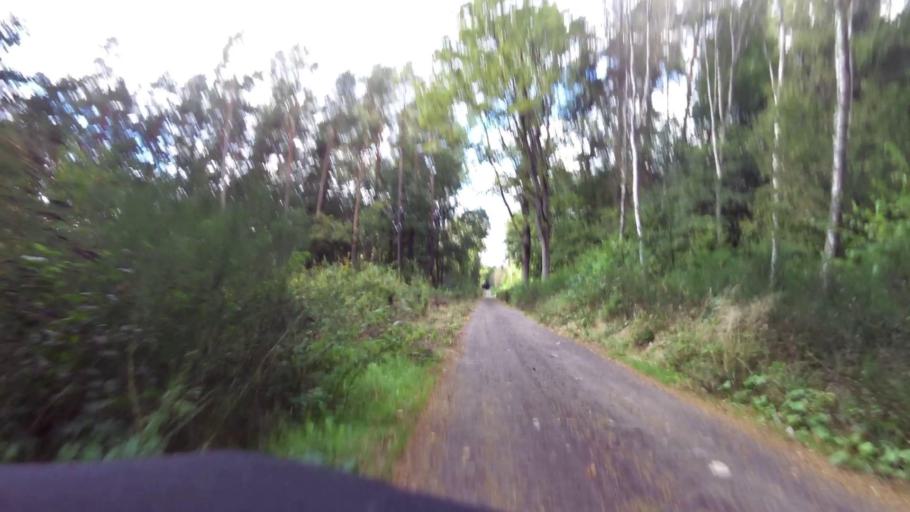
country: PL
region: West Pomeranian Voivodeship
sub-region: Koszalin
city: Koszalin
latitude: 54.0541
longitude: 16.1299
